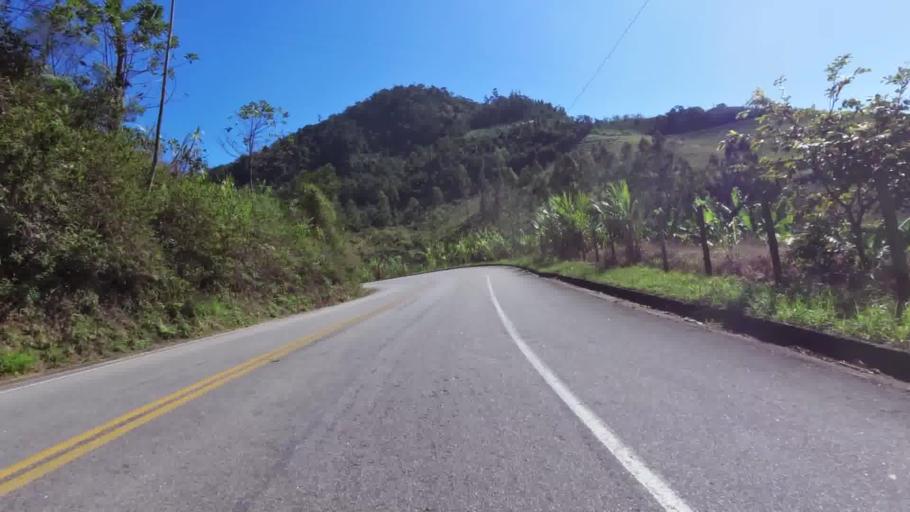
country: BR
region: Espirito Santo
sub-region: Vargem Alta
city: Vargem Alta
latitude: -20.6966
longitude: -40.9359
